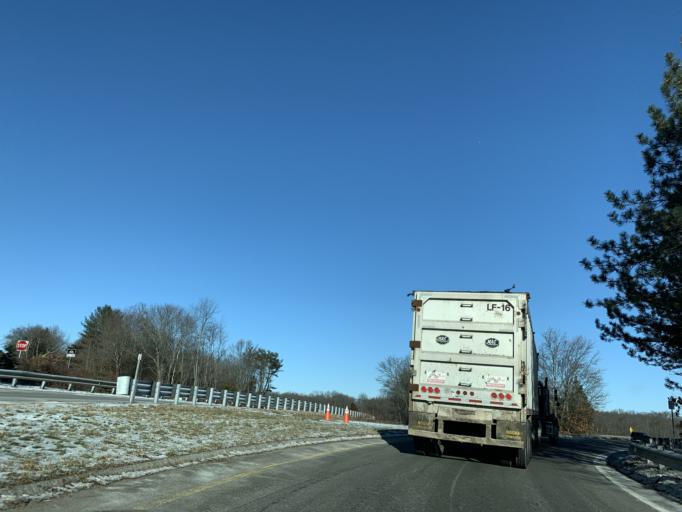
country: US
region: Massachusetts
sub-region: Norfolk County
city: Dedham
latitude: 42.2126
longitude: -71.1517
